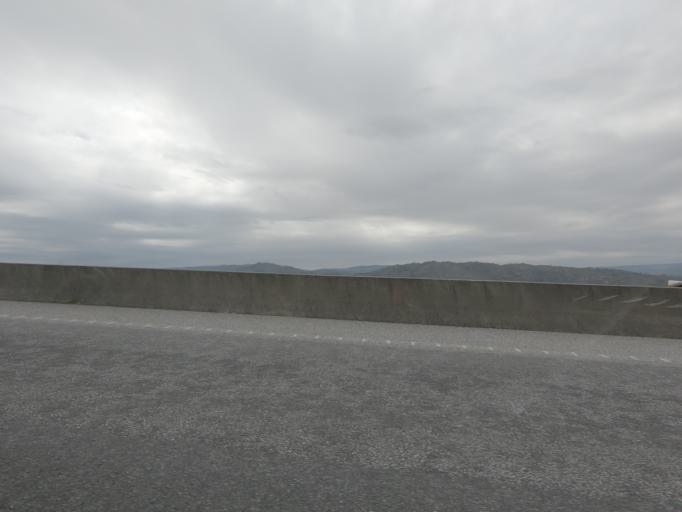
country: PT
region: Guarda
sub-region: Guarda
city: Guarda
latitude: 40.5961
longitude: -7.2760
